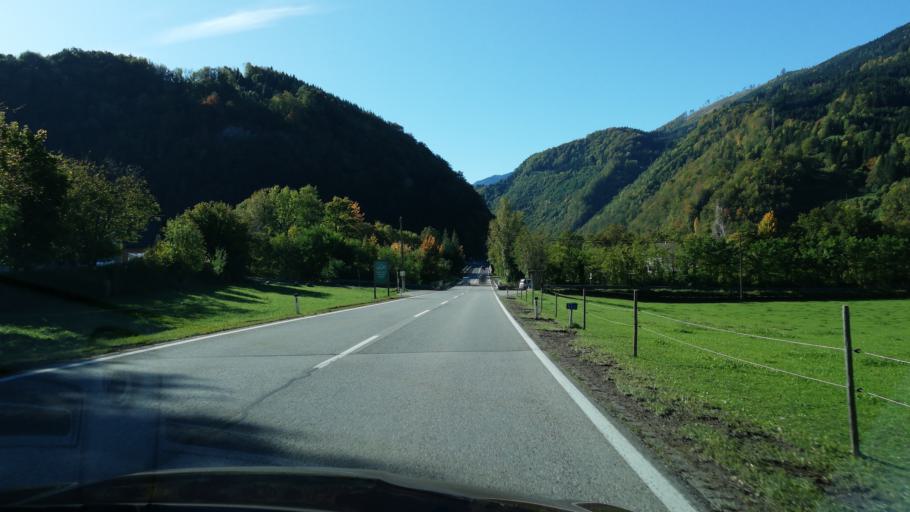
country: AT
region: Upper Austria
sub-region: Politischer Bezirk Steyr-Land
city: Weyer
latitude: 47.8553
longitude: 14.6416
